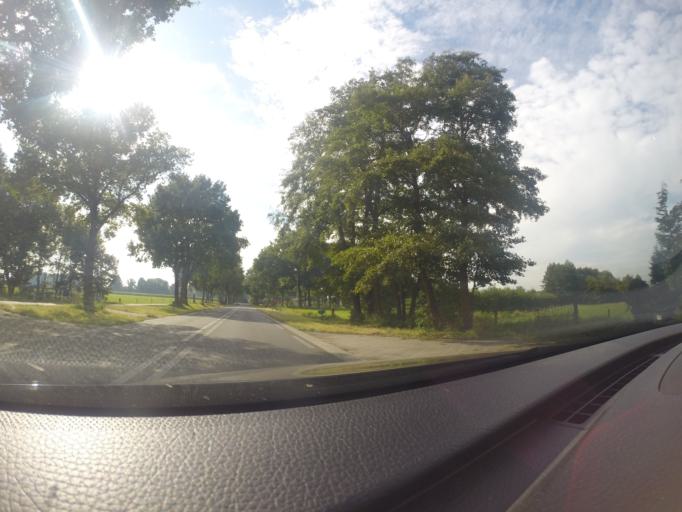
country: NL
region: Gelderland
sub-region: Gemeente Bronckhorst
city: Zelhem
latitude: 51.9909
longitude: 6.3428
